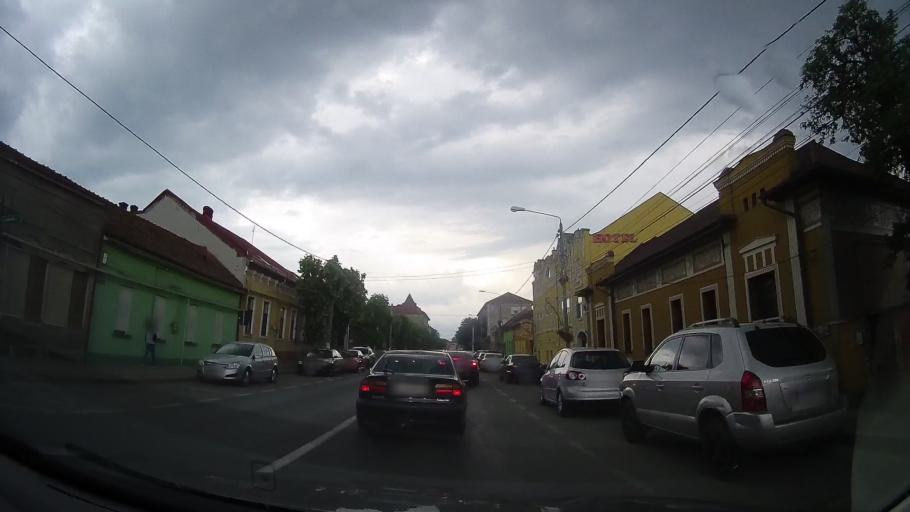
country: RO
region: Caras-Severin
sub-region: Municipiul Caransebes
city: Caransebes
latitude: 45.4113
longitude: 22.2139
